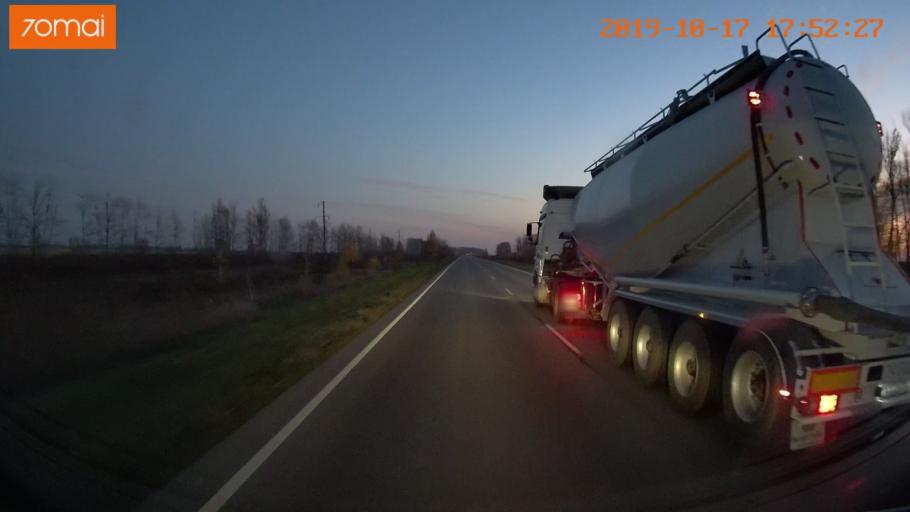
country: RU
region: Tula
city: Kurkino
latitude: 53.6348
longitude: 38.6838
